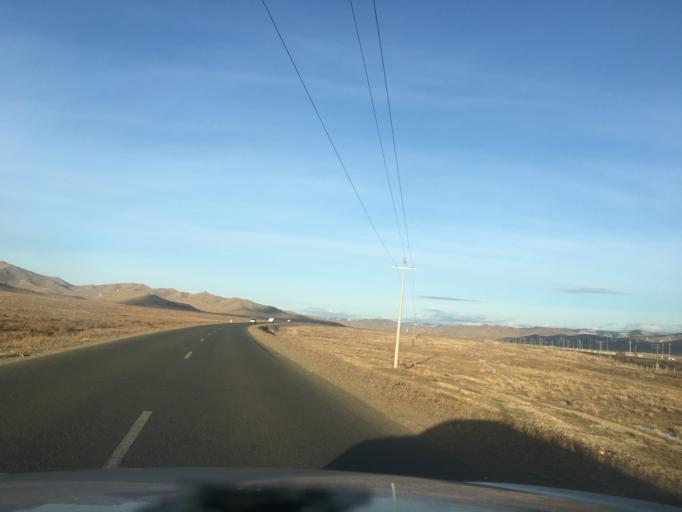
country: MN
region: Central Aimak
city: Ihsueuej
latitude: 48.0809
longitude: 106.5852
